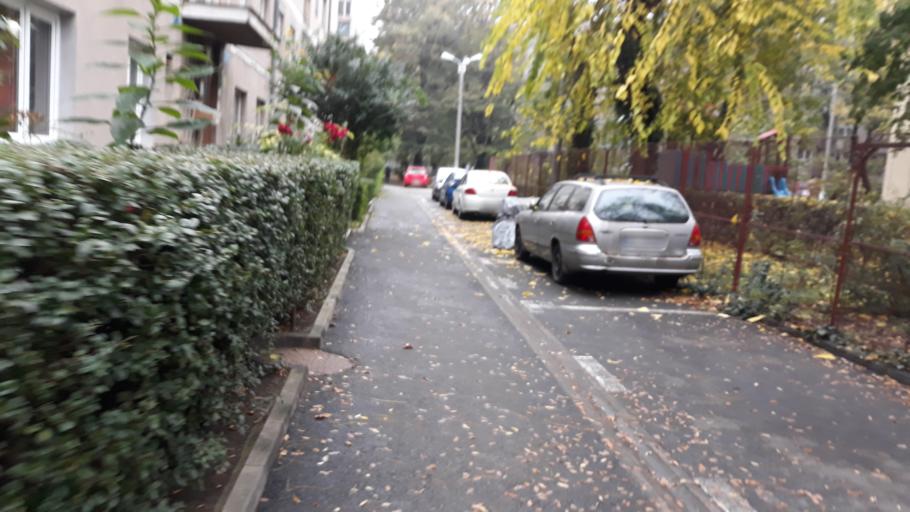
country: RO
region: Bihor
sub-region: Comuna Biharea
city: Oradea
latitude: 47.0510
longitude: 21.9365
